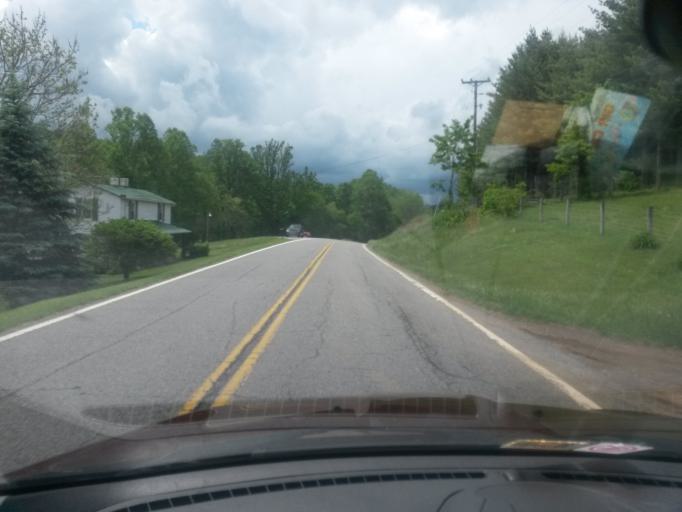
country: US
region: Virginia
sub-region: Floyd County
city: Floyd
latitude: 36.8661
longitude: -80.3314
